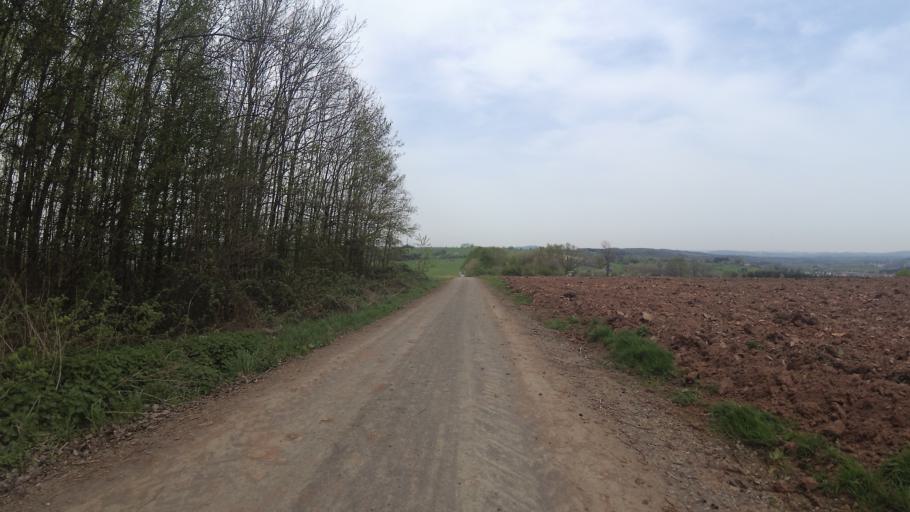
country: DE
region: Saarland
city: Mainzweiler
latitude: 49.4057
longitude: 7.1162
